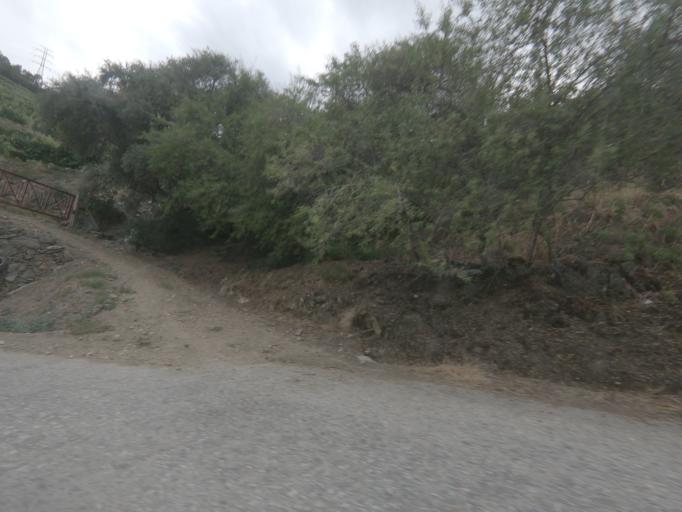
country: PT
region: Viseu
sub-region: Armamar
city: Armamar
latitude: 41.1261
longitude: -7.6430
